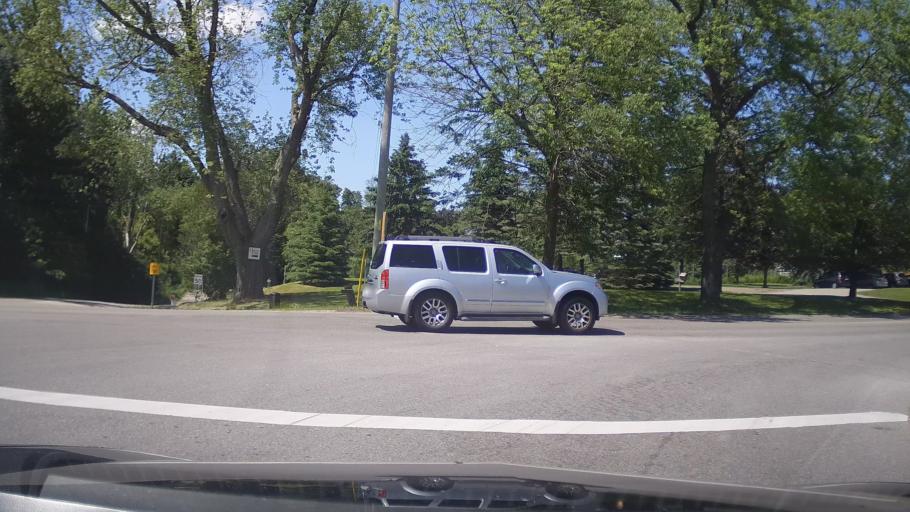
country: CA
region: Ontario
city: Oshawa
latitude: 43.9937
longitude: -78.8624
